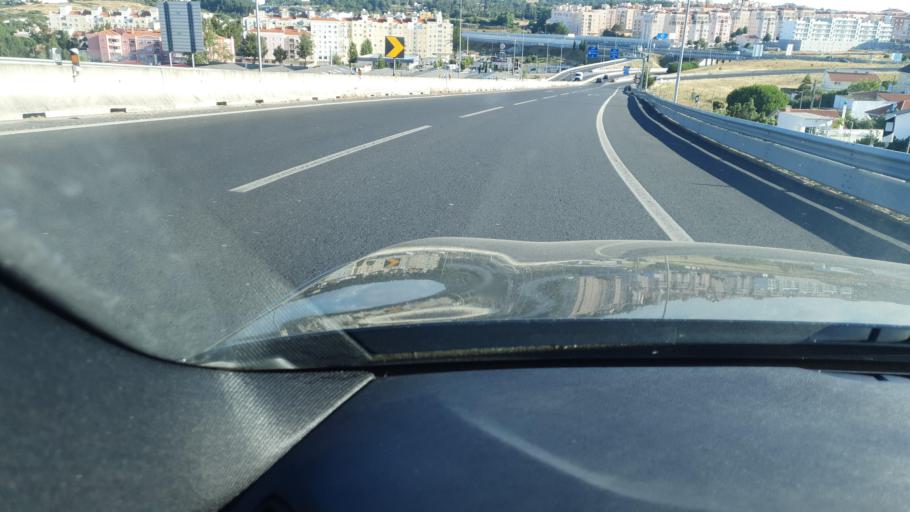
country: PT
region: Lisbon
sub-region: Sintra
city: Cacem
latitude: 38.7708
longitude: -9.2818
